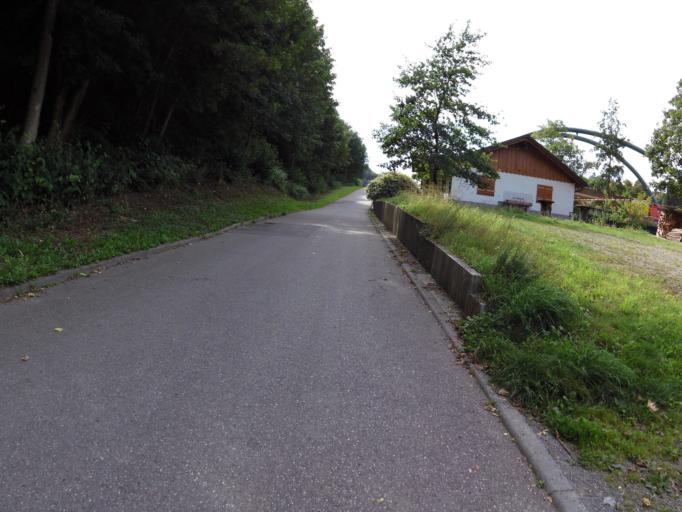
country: DE
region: Baden-Wuerttemberg
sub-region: Freiburg Region
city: Sulz am Neckar
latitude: 48.3668
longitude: 8.6416
